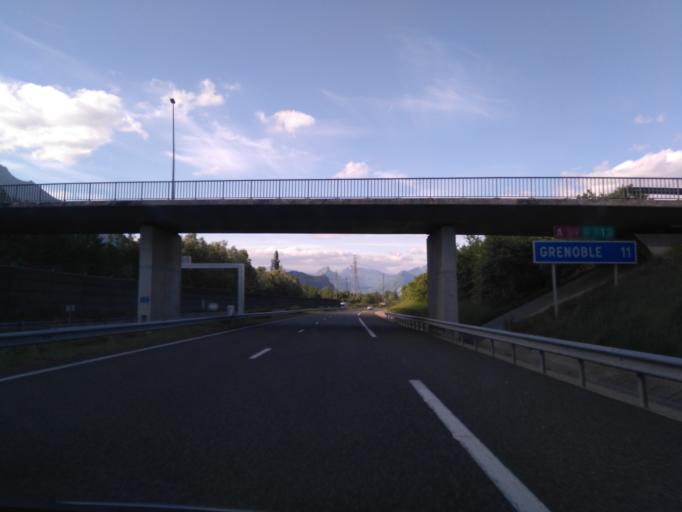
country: FR
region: Rhone-Alpes
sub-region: Departement de l'Isere
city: Allieres-et-Risset
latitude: 45.0933
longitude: 5.6701
